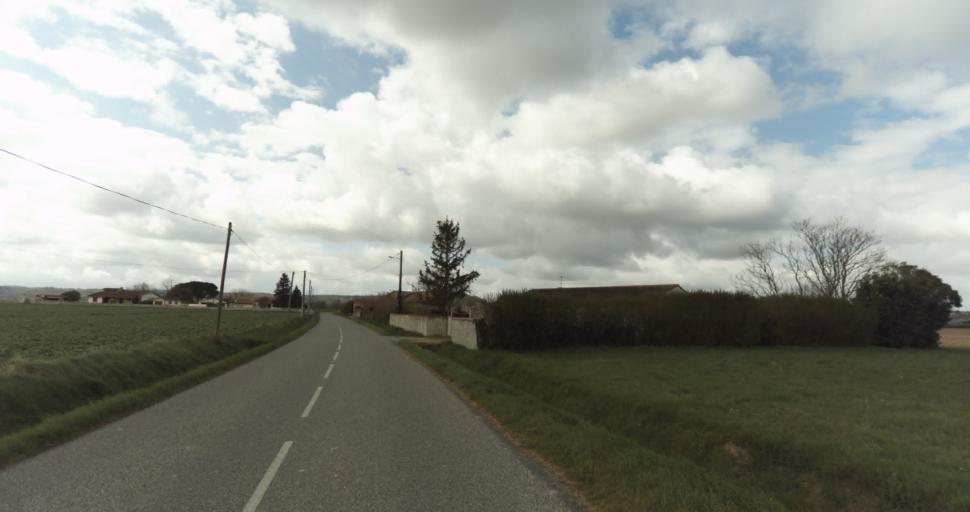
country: FR
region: Midi-Pyrenees
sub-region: Departement de la Haute-Garonne
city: Auterive
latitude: 43.3383
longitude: 1.4586
